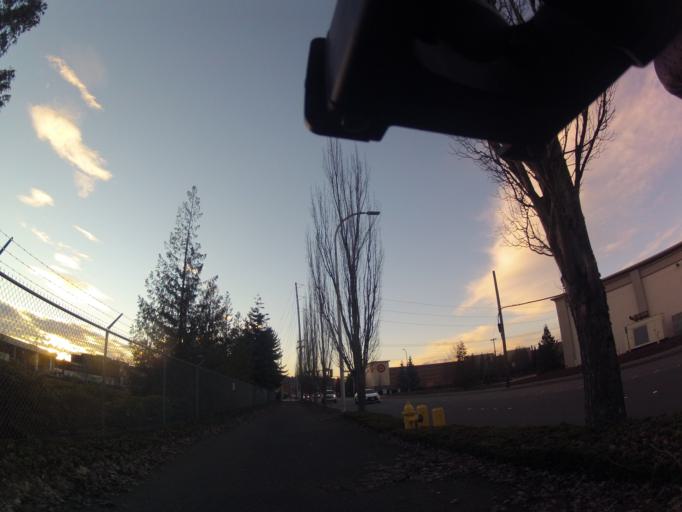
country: US
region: Washington
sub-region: King County
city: Renton
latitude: 47.4956
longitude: -122.1962
